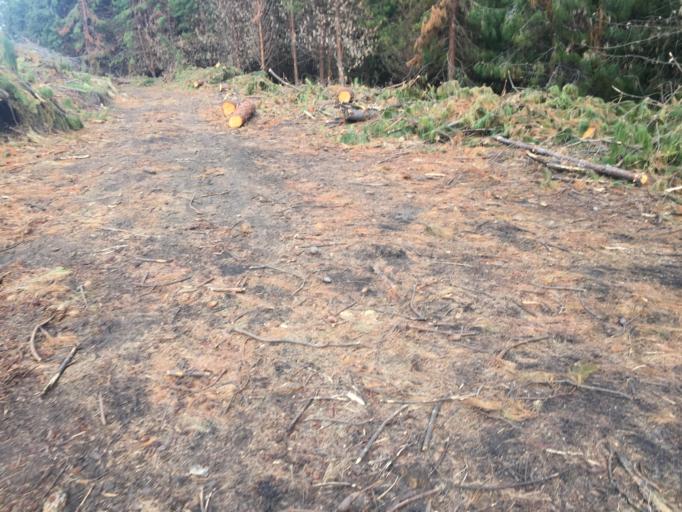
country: EC
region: Imbabura
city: Ibarra
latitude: 0.2259
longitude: -78.1246
